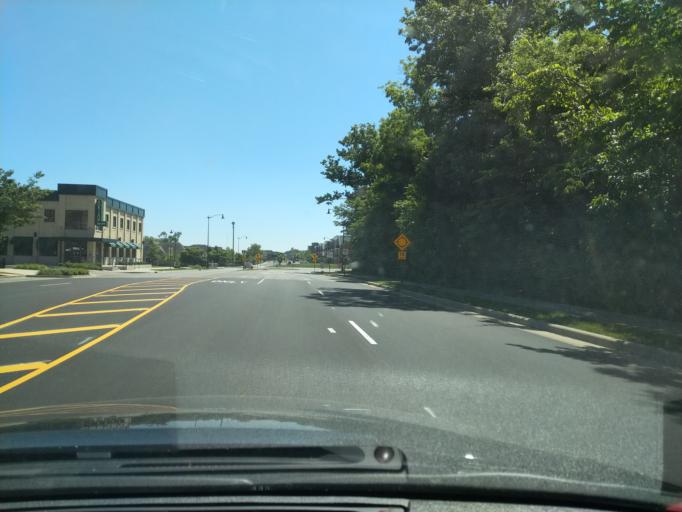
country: US
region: Indiana
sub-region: Hamilton County
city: Carmel
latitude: 39.9717
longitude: -86.1517
